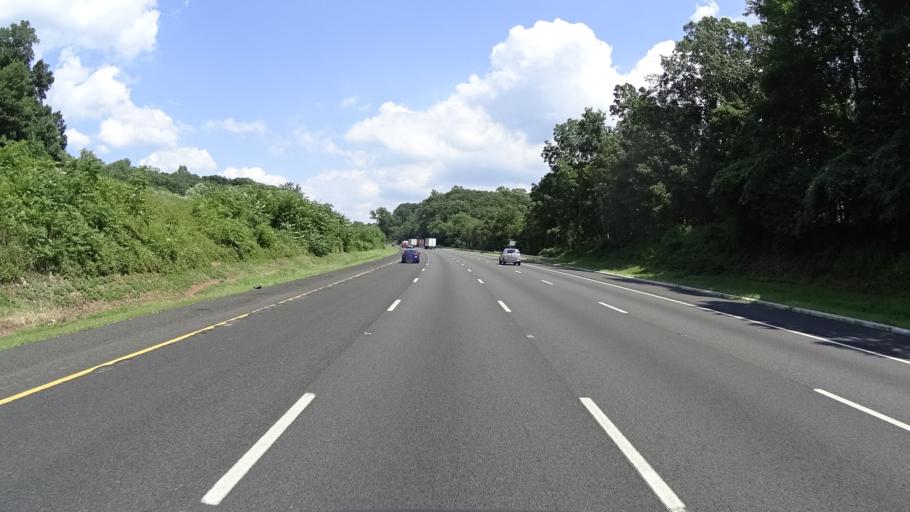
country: US
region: New Jersey
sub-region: Somerset County
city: Green Knoll
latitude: 40.6429
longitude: -74.6180
